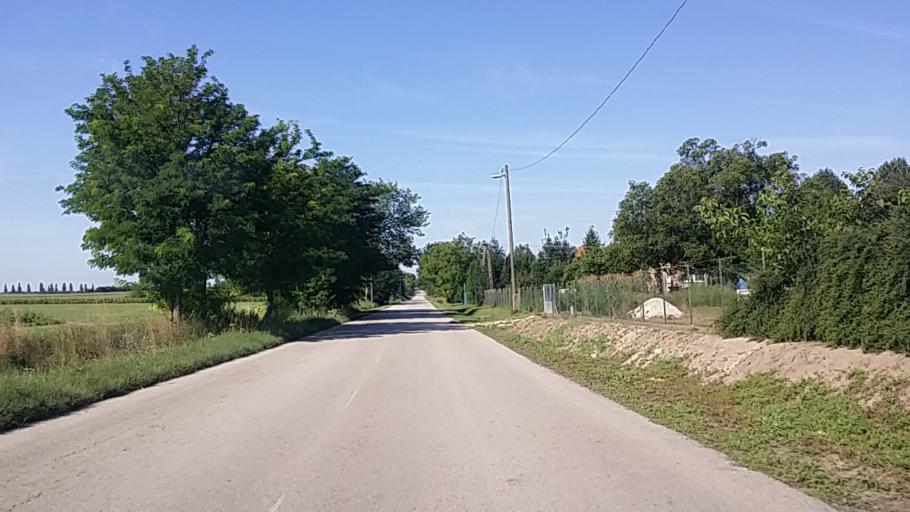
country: HU
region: Fejer
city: Ivancsa
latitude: 47.1389
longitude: 18.8346
